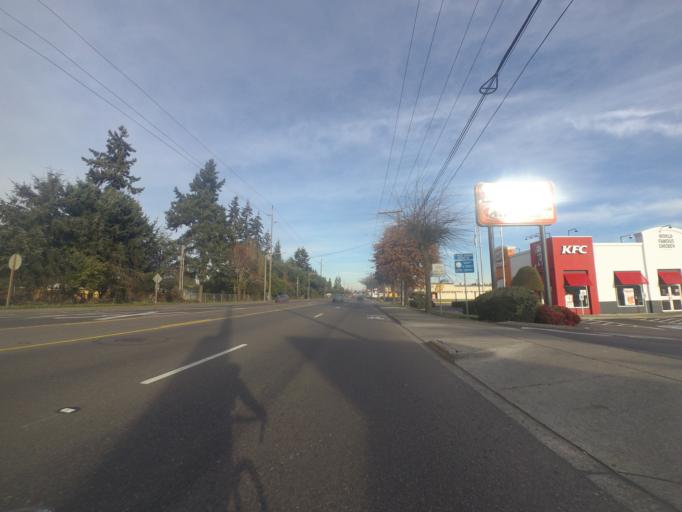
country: US
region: Washington
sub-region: Pierce County
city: McChord Air Force Base
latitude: 47.1504
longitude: -122.5043
